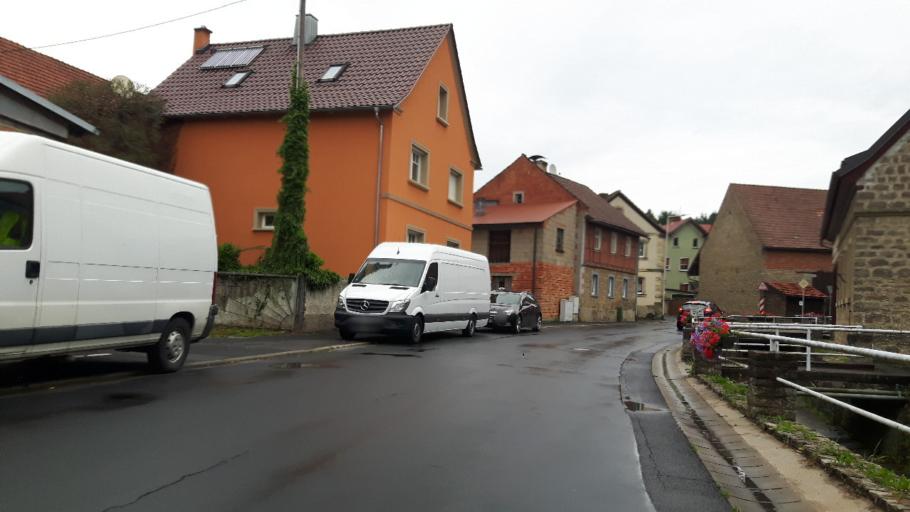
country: DE
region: Bavaria
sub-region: Regierungsbezirk Unterfranken
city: Uchtelhausen
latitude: 50.0945
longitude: 10.2486
